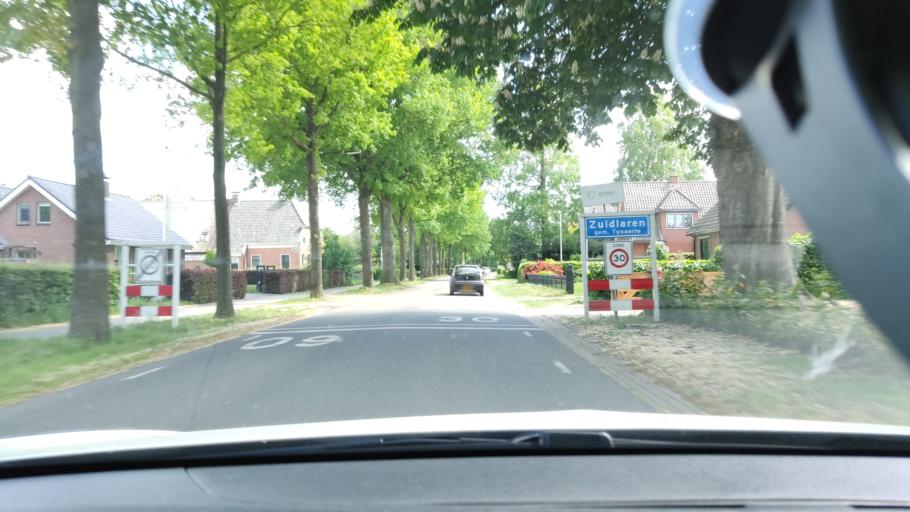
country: NL
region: Drenthe
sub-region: Gemeente Tynaarlo
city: Zuidlaren
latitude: 53.1013
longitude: 6.6882
